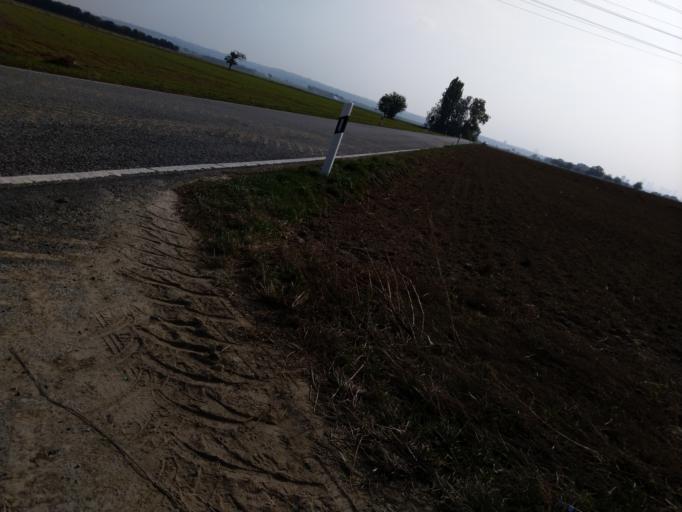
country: DE
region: Hesse
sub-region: Regierungsbezirk Darmstadt
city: Friedrichsdorf
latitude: 50.2154
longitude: 8.6792
